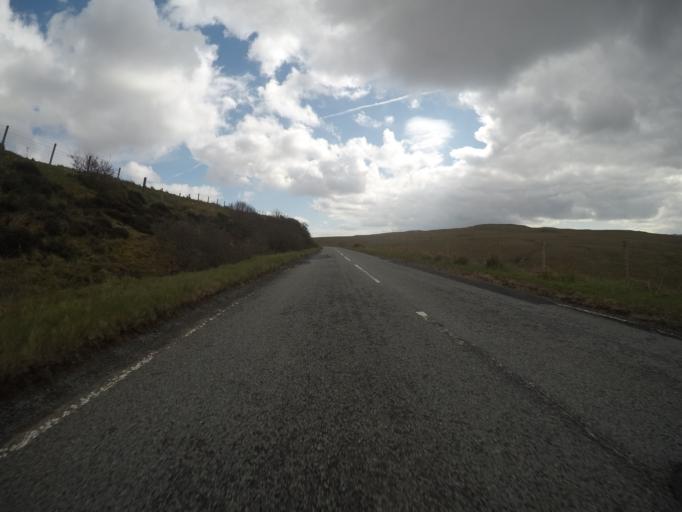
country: GB
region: Scotland
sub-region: Highland
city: Isle of Skye
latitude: 57.3275
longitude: -6.3335
